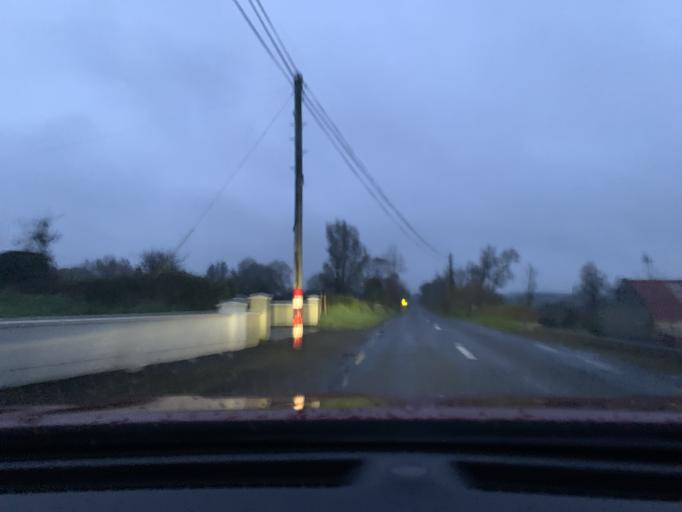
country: IE
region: Connaught
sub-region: Sligo
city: Ballymote
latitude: 54.0552
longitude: -8.5208
